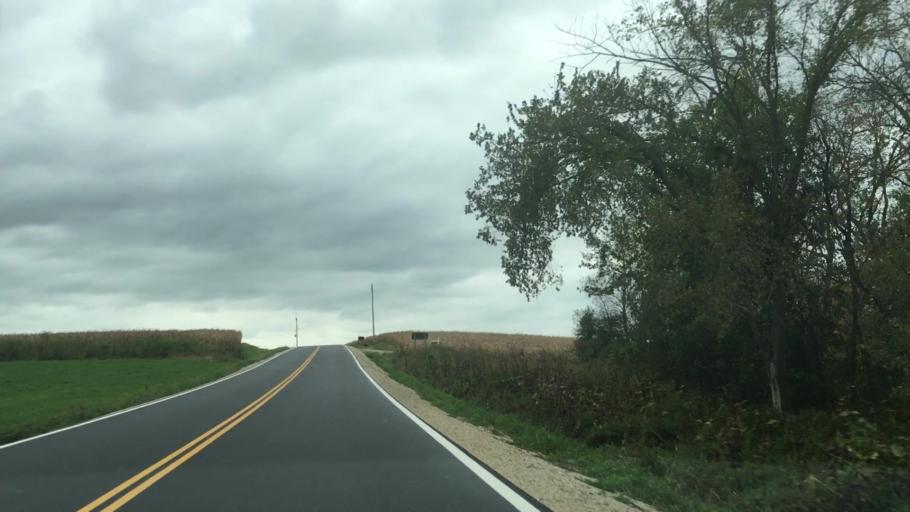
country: US
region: Minnesota
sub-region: Fillmore County
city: Preston
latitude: 43.7596
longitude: -92.0136
